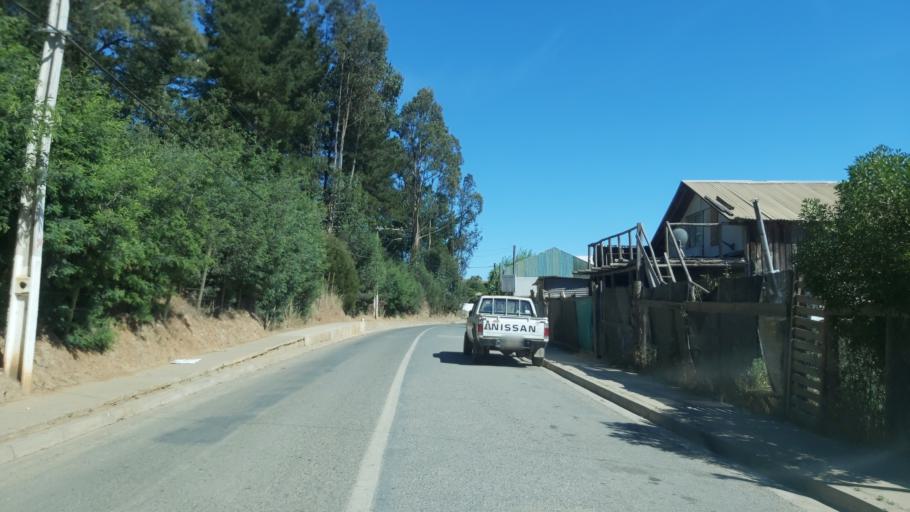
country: CL
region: Maule
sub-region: Provincia de Talca
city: Constitucion
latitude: -34.7729
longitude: -72.0662
